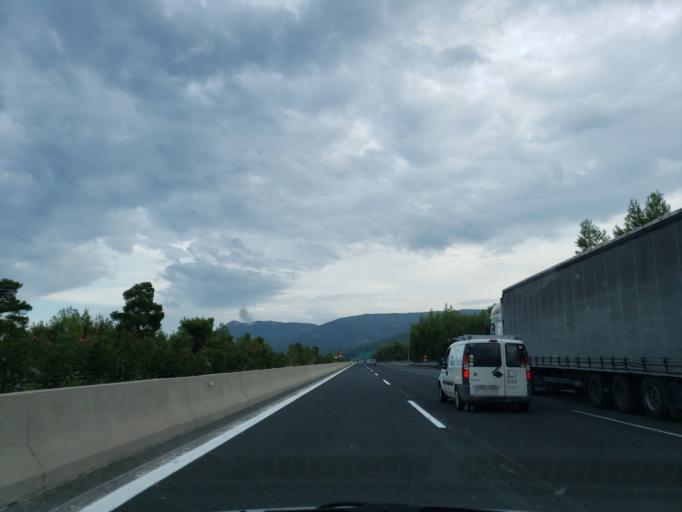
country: GR
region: Attica
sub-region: Nomarchia Anatolikis Attikis
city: Oropos
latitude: 38.2474
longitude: 23.7669
